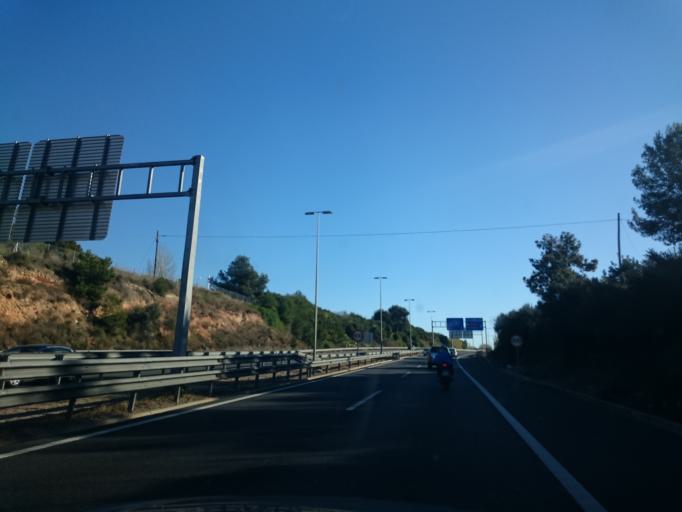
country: ES
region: Catalonia
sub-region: Provincia de Tarragona
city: Tarragona
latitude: 41.1244
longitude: 1.2479
